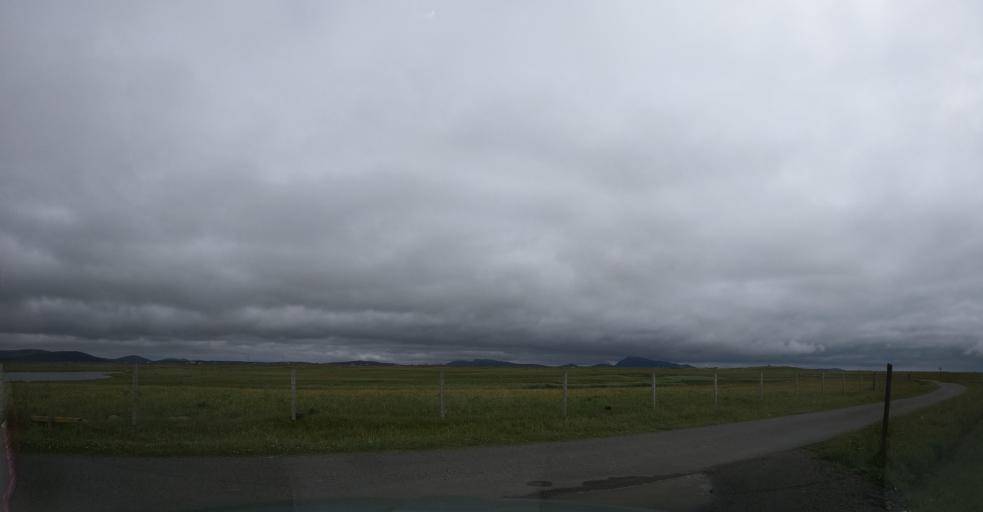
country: GB
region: Scotland
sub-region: Eilean Siar
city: Isle of North Uist
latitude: 57.5305
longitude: -7.3842
